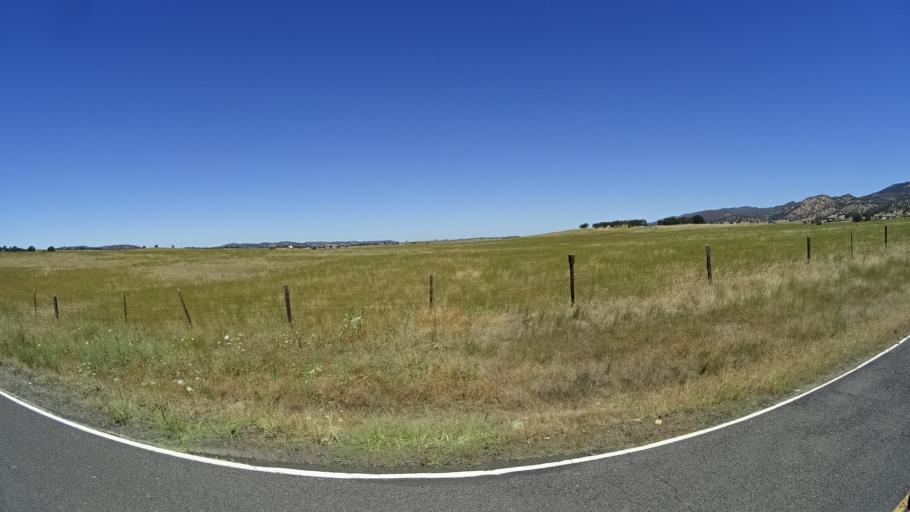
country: US
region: California
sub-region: Calaveras County
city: Copperopolis
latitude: 38.0223
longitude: -120.6945
